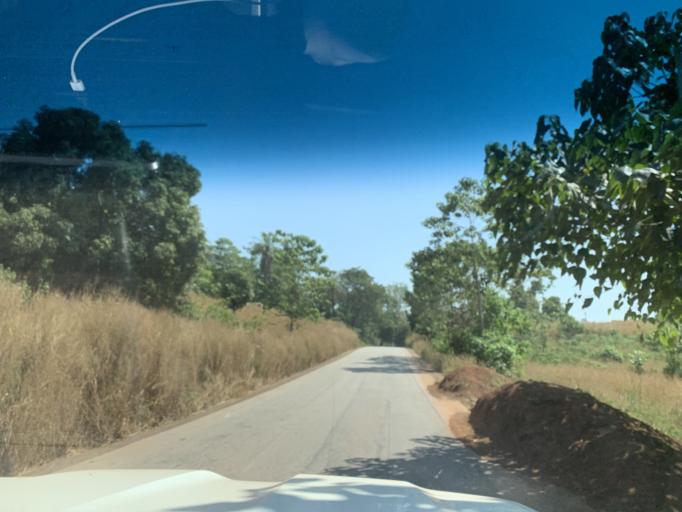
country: GN
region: Kindia
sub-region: Kindia
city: Kindia
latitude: 10.0962
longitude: -12.6213
